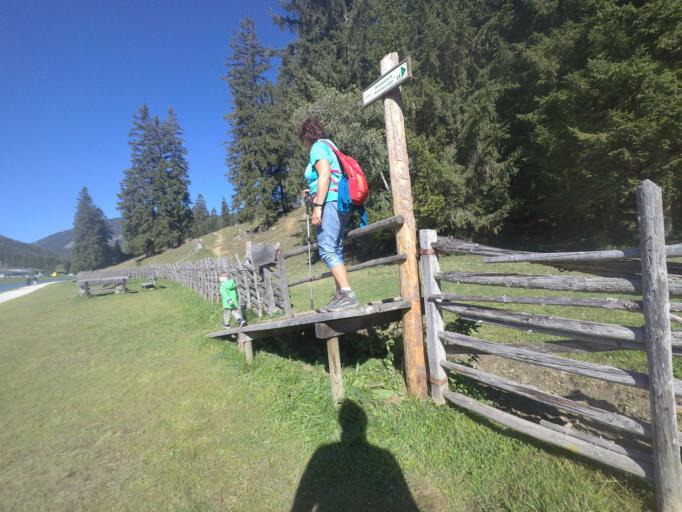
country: AT
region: Styria
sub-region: Politischer Bezirk Weiz
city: Passail
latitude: 47.3498
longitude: 15.4647
